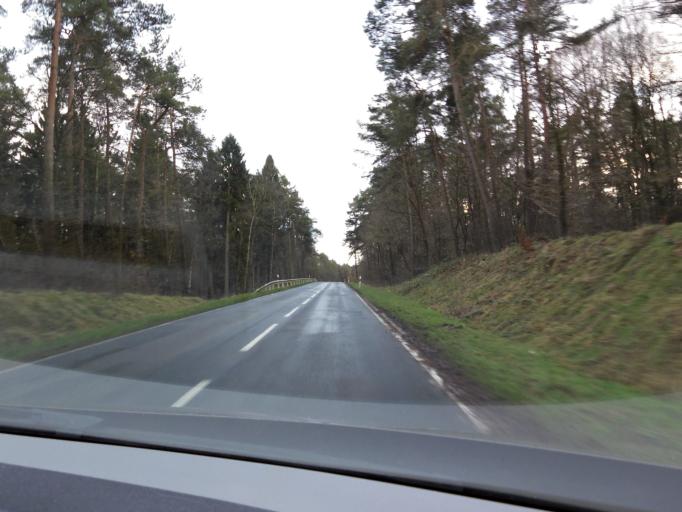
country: DE
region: Schleswig-Holstein
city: Seedorf
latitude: 53.6449
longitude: 10.8613
